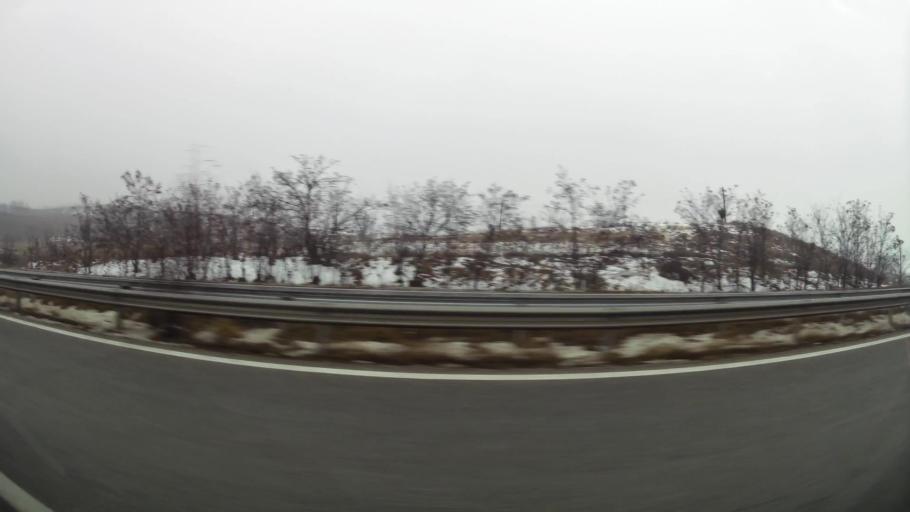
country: MK
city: Miladinovci
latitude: 41.9742
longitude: 21.6492
